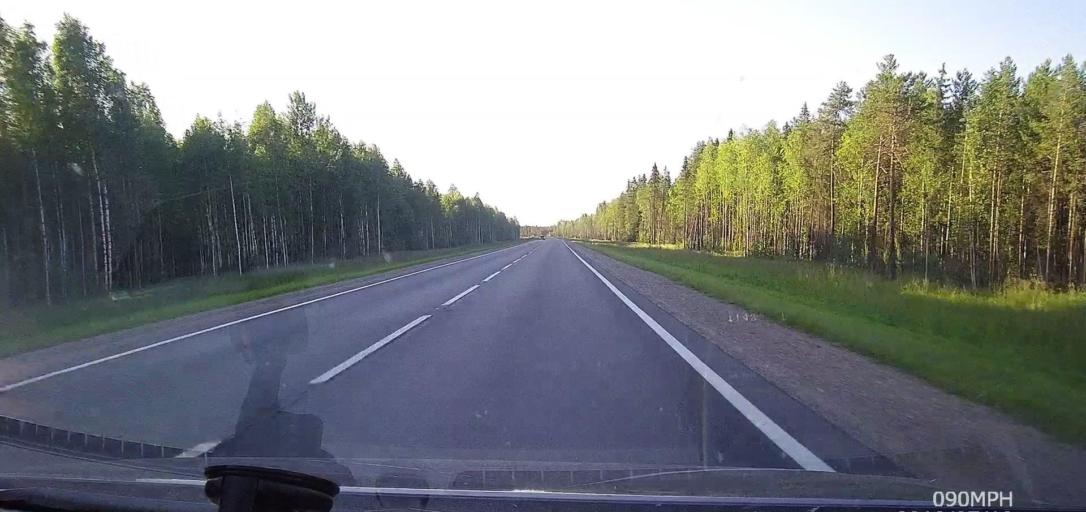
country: RU
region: Arkhangelskaya
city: Kholmogory
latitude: 64.1222
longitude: 41.6631
